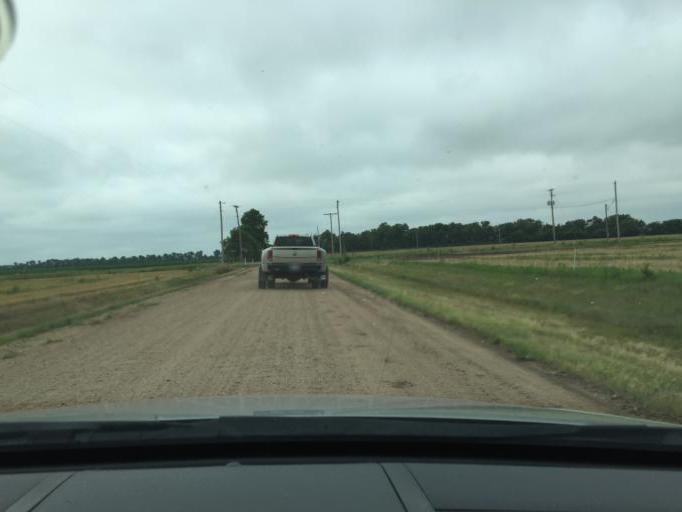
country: US
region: Kansas
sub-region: Reno County
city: South Hutchinson
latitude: 37.9710
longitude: -98.0319
